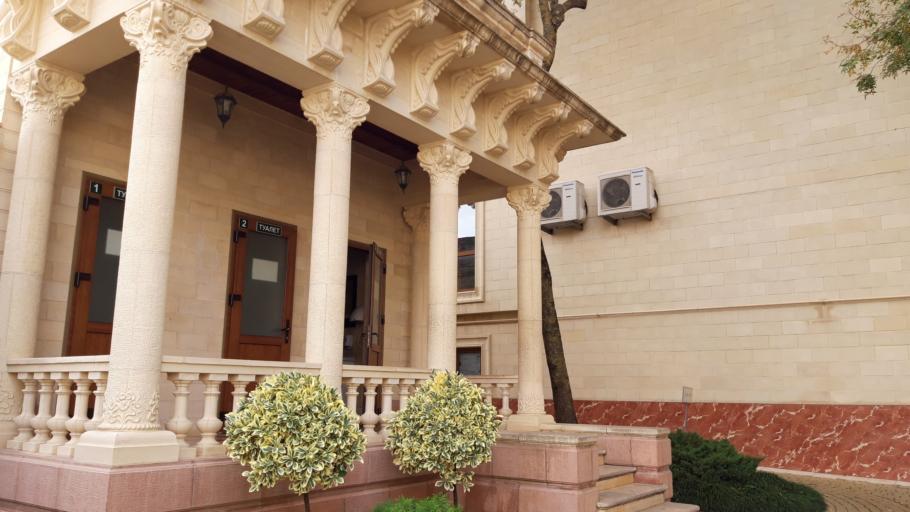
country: RU
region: Krasnodarskiy
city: Kabardinka
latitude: 44.6443
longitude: 37.9357
